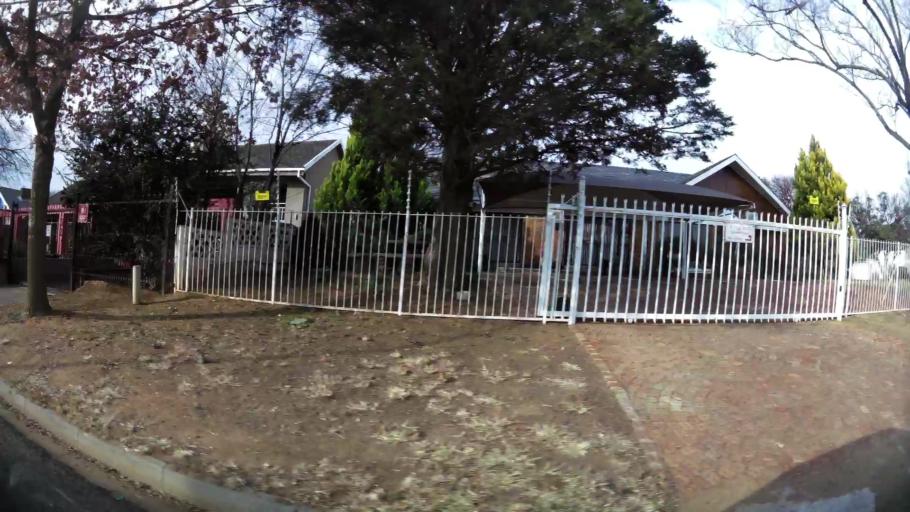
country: ZA
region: Orange Free State
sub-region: Mangaung Metropolitan Municipality
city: Bloemfontein
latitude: -29.1237
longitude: 26.1787
